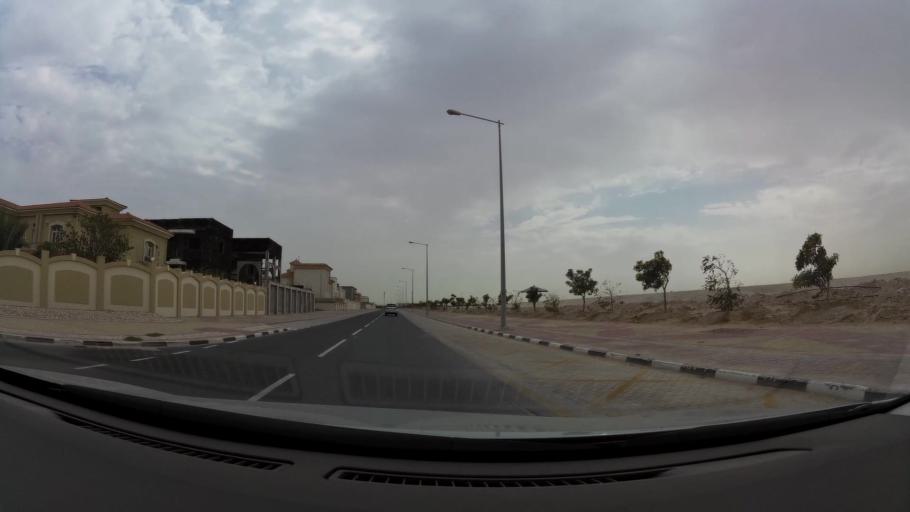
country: QA
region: Baladiyat ad Dawhah
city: Doha
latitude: 25.3542
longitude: 51.4931
